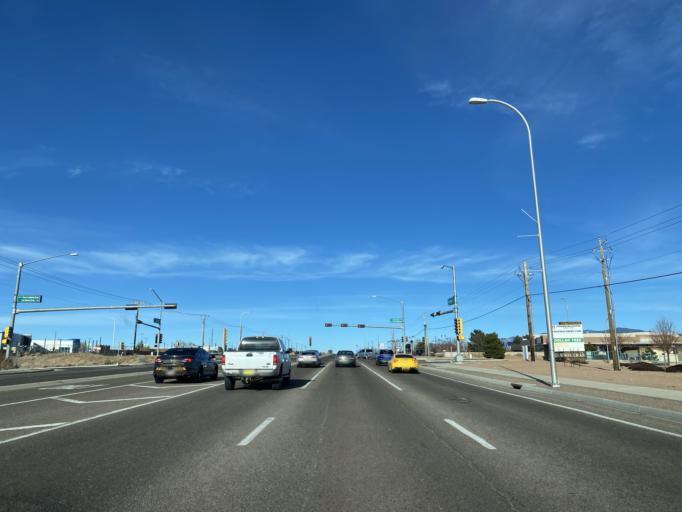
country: US
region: New Mexico
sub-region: Santa Fe County
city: Agua Fria
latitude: 35.6197
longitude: -106.0291
